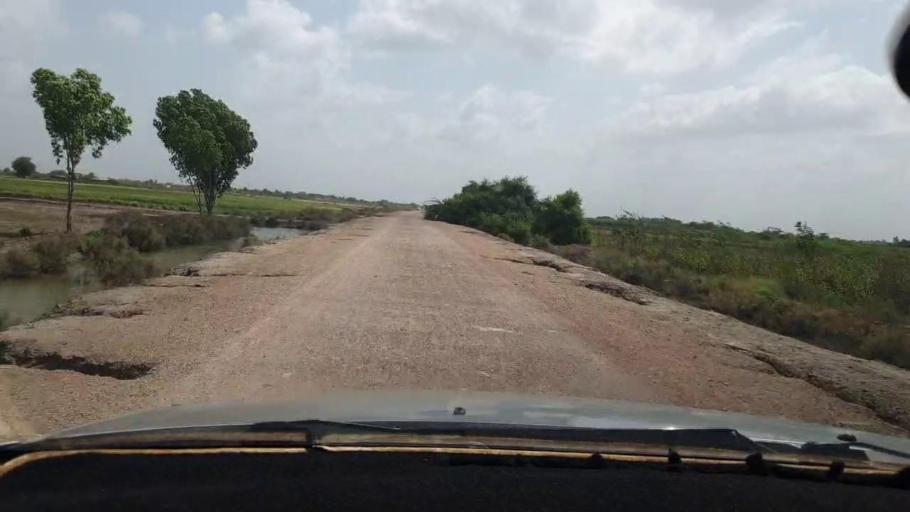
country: PK
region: Sindh
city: Tando Bago
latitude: 24.7207
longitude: 69.1812
